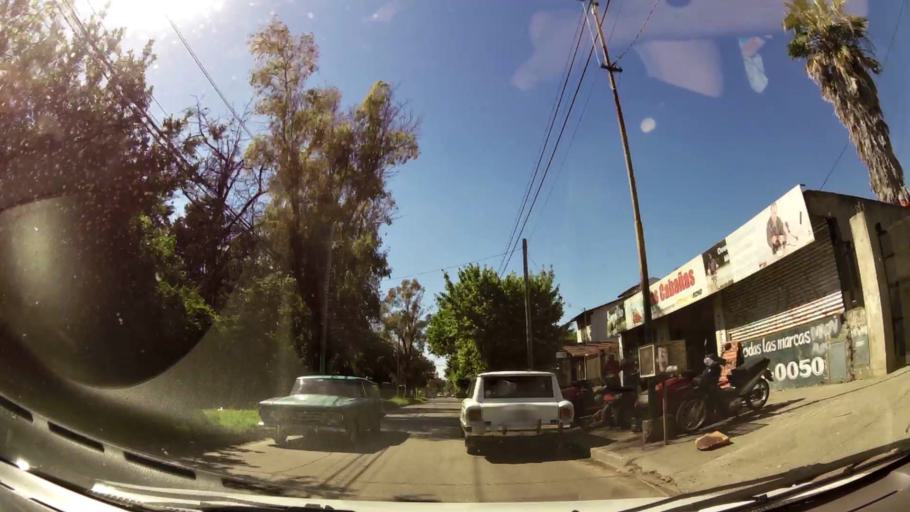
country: AR
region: Buenos Aires
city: Ituzaingo
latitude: -34.6263
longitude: -58.6586
